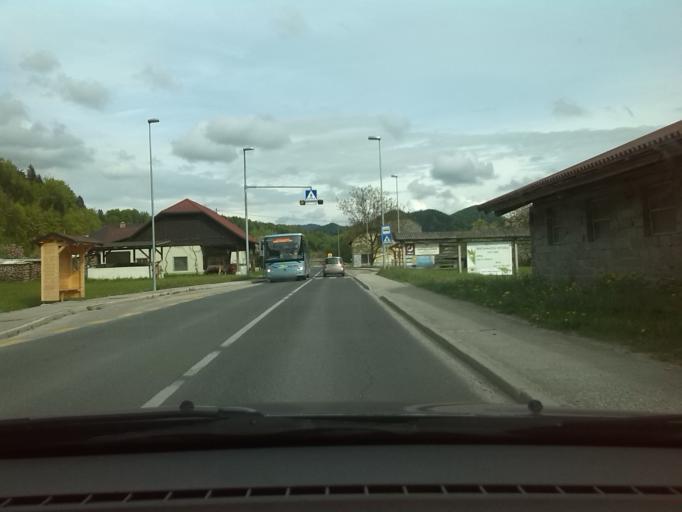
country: SI
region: Lukovica
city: Lukovica pri Domzalah
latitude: 46.2253
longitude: 14.6830
